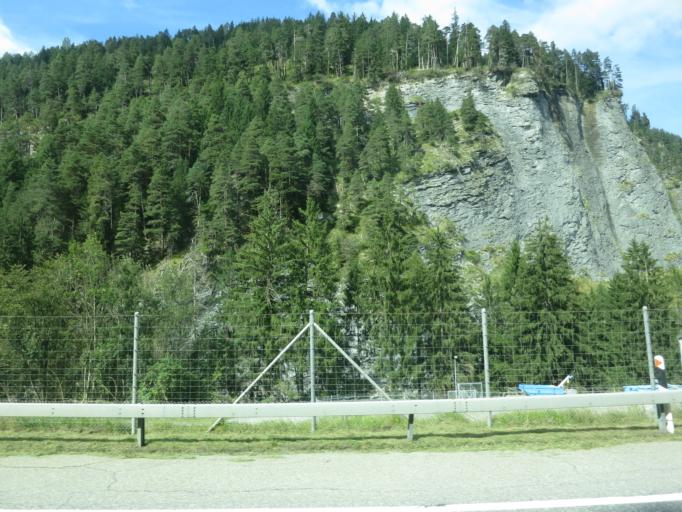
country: CH
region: Grisons
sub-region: Hinterrhein District
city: Thusis
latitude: 46.6438
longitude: 9.4462
